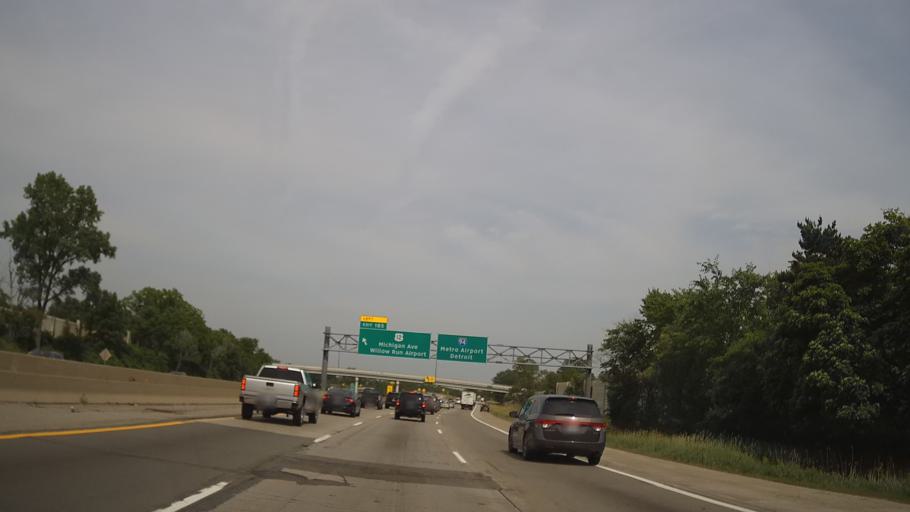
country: US
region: Michigan
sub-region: Washtenaw County
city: Ypsilanti
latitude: 42.2316
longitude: -83.5866
